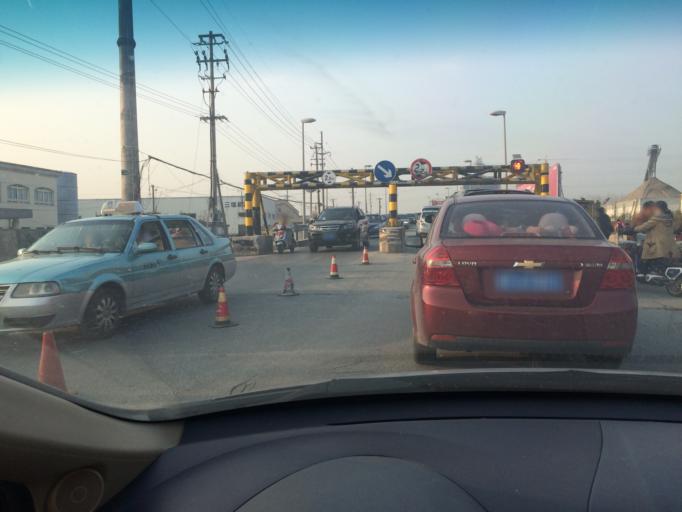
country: CN
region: Jiangsu Sheng
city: Guoxiang
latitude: 31.2592
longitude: 120.6700
